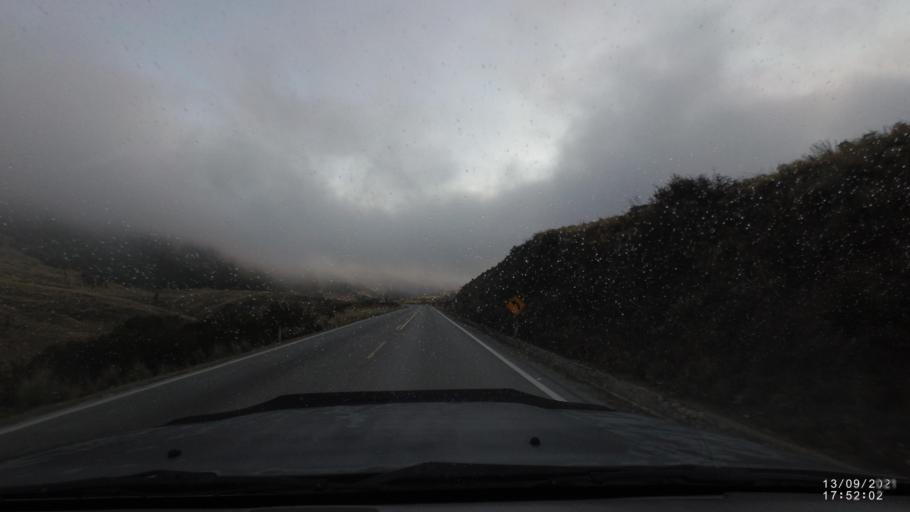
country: BO
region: Cochabamba
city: Colomi
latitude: -17.4015
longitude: -65.8775
